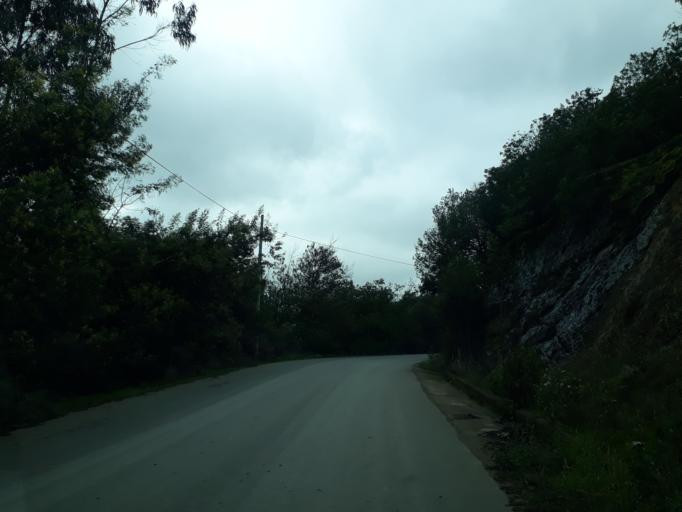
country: CO
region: Cundinamarca
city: Cucunuba
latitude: 5.1929
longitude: -73.7881
